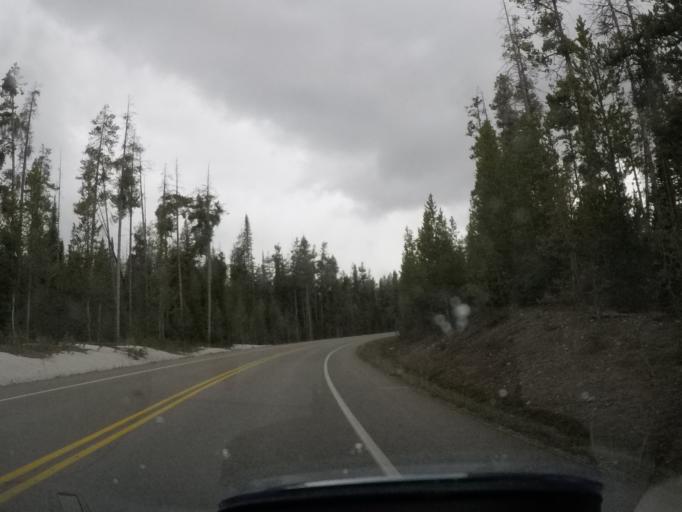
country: US
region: Wyoming
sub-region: Teton County
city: Moose Wilson Road
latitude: 44.0073
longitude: -110.6889
